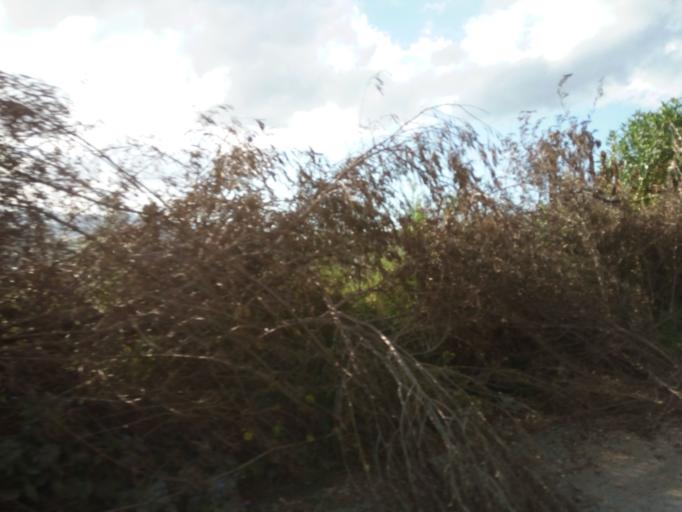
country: DZ
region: Tipaza
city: Hadjout
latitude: 36.3733
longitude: 2.4804
